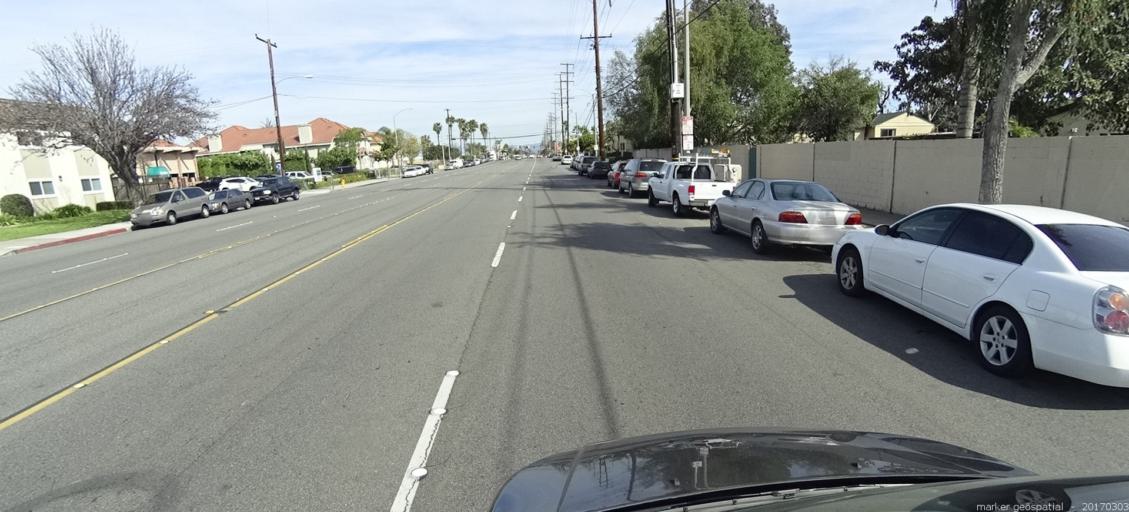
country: US
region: California
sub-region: Orange County
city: Cypress
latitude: 33.8172
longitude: -118.0144
